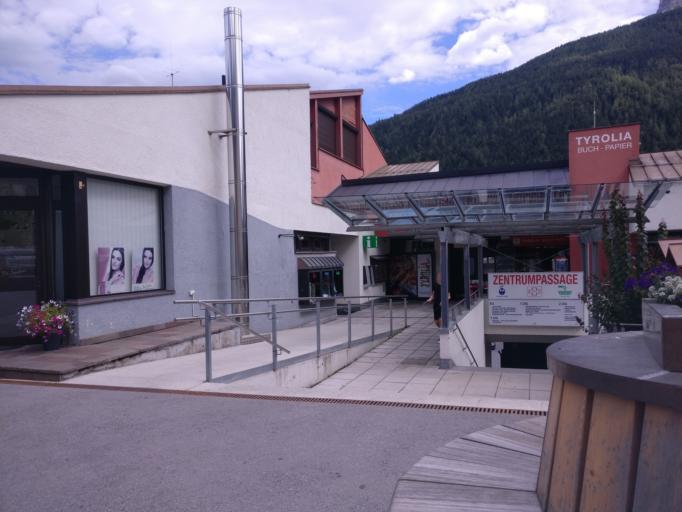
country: AT
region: Tyrol
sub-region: Politischer Bezirk Innsbruck Land
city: Fulpmes
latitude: 47.1532
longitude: 11.3486
